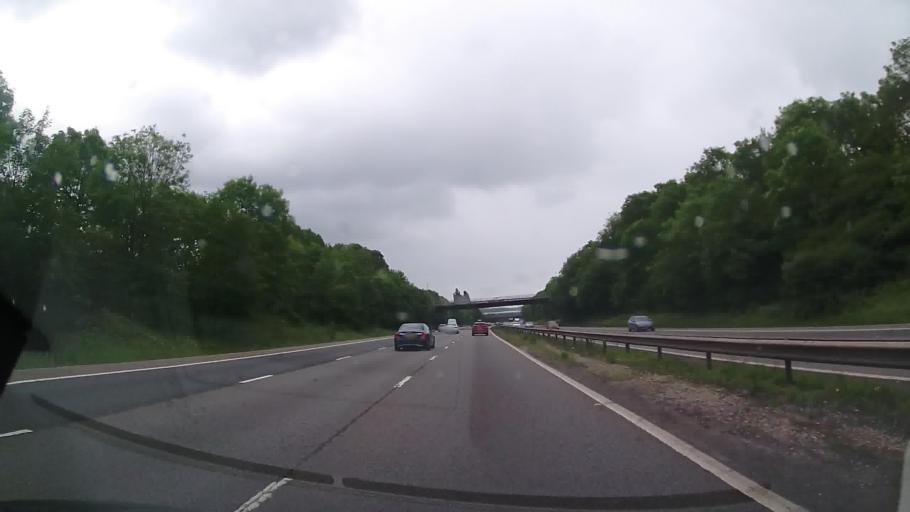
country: GB
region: England
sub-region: Leicestershire
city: Kirby Muxloe
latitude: 52.6536
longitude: -1.2413
